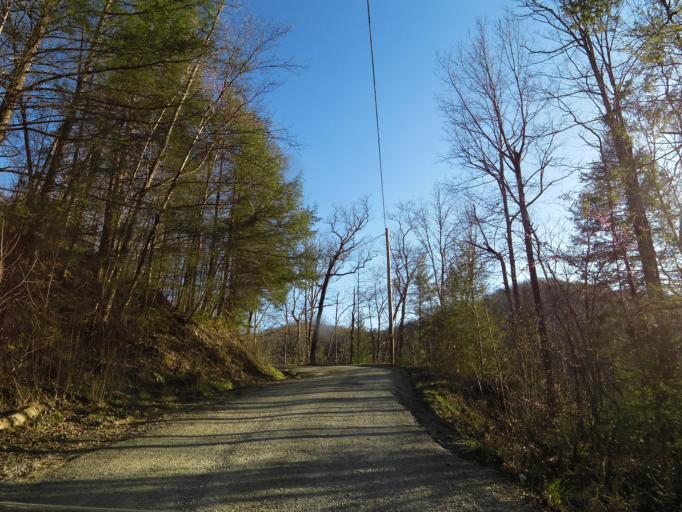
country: US
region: Tennessee
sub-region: Campbell County
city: Caryville
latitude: 36.2607
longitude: -84.3513
